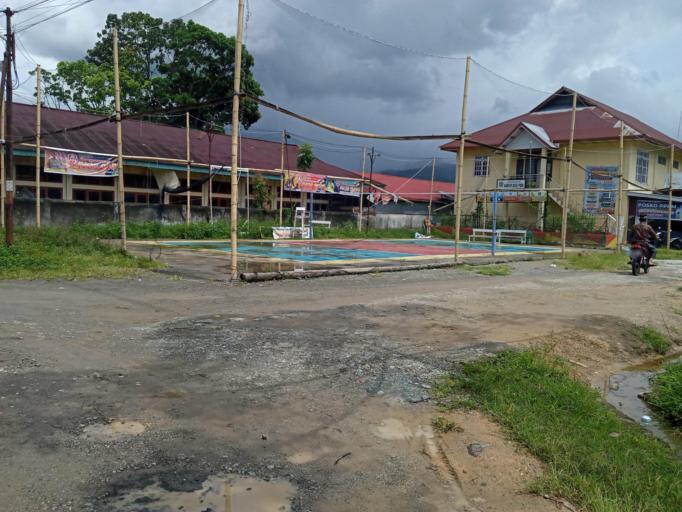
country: ID
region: Jambi
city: Semurup
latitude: -1.9901
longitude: 101.3700
